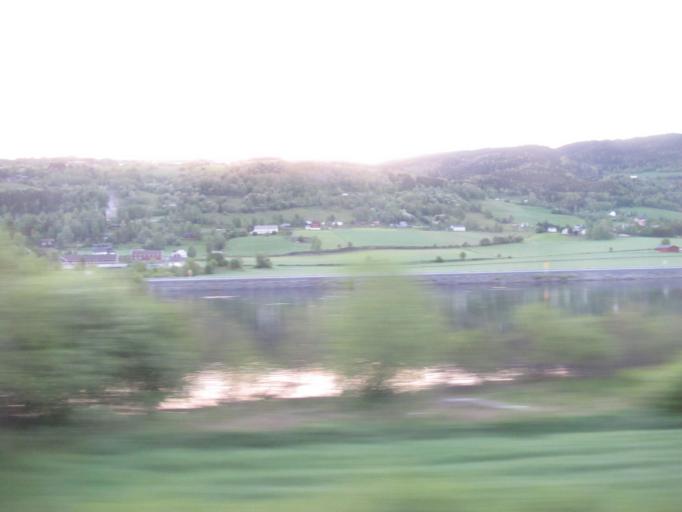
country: NO
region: Oppland
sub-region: Oyer
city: Tretten
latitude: 61.2583
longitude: 10.4161
